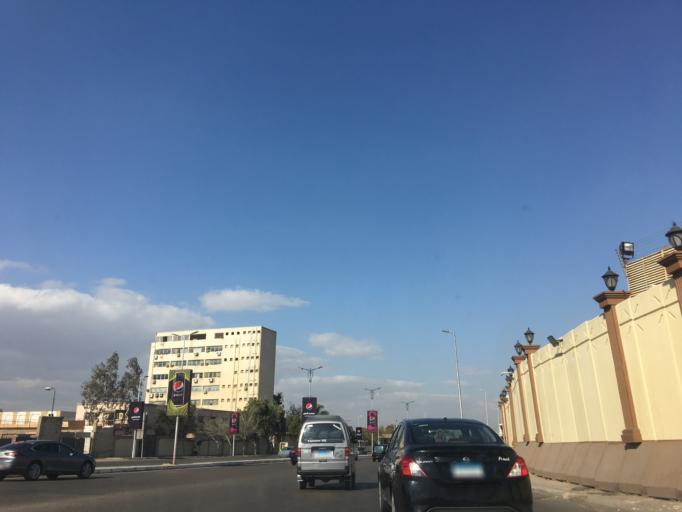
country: EG
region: Muhafazat al Qahirah
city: Cairo
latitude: 30.0511
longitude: 31.3076
